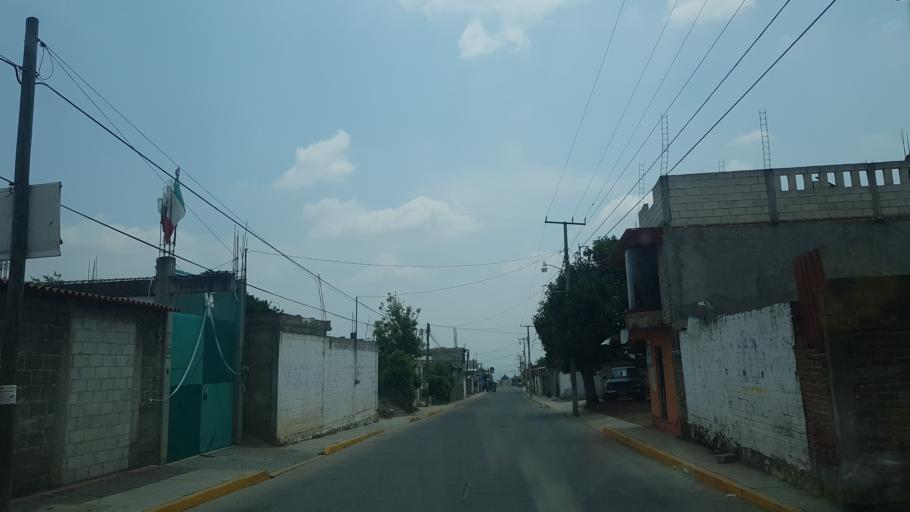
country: MX
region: Puebla
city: Domingo Arenas
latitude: 19.1394
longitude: -98.4538
